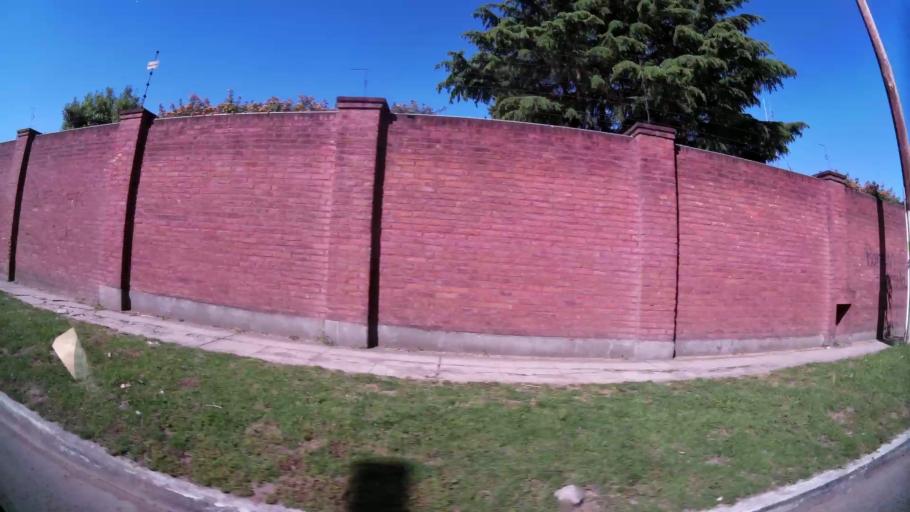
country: AR
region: Buenos Aires
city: Santa Catalina - Dique Lujan
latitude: -34.4755
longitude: -58.7048
